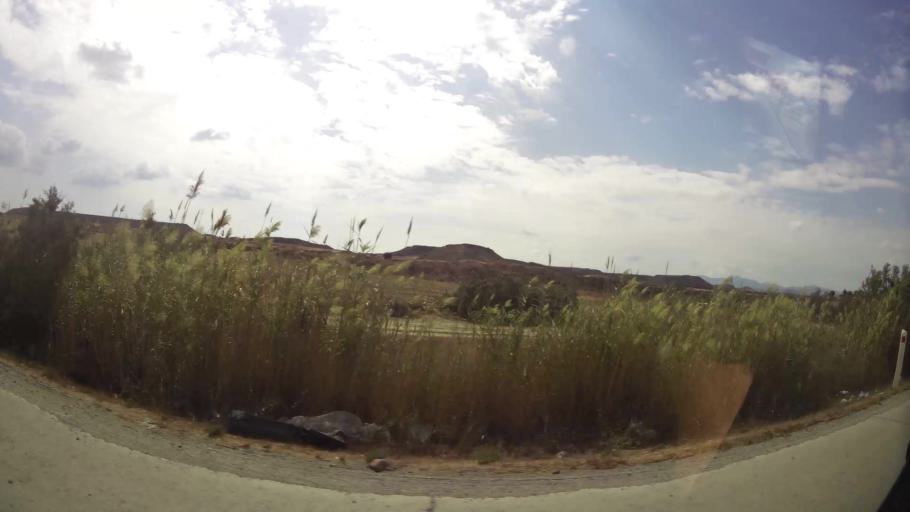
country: CY
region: Lefkosia
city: Tseri
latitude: 35.0593
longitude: 33.3574
